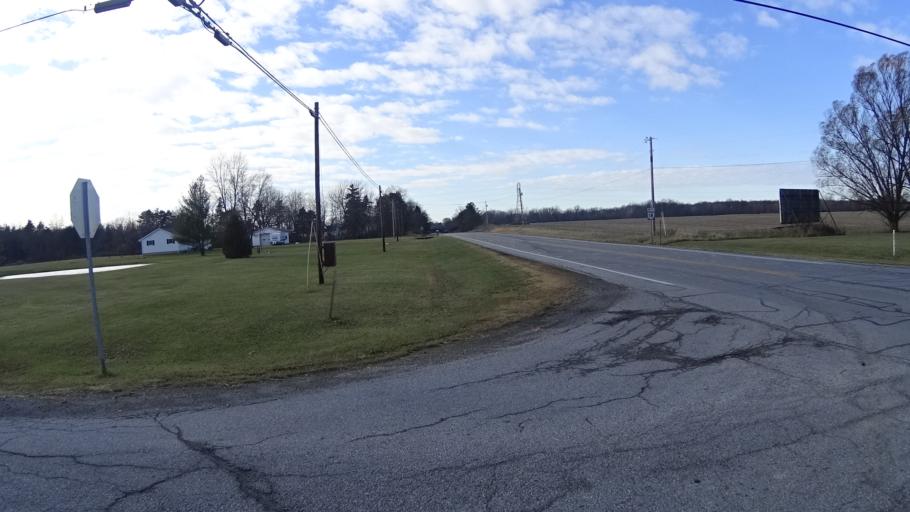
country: US
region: Ohio
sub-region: Lorain County
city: Wellington
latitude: 41.1693
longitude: -82.2688
